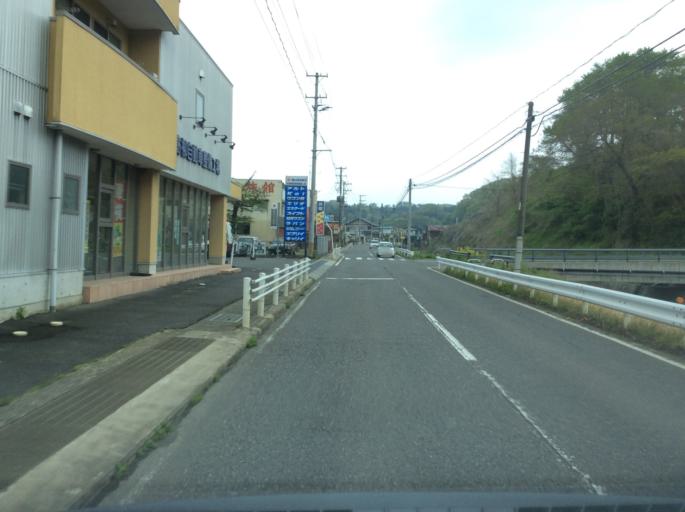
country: JP
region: Fukushima
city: Miharu
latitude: 37.4408
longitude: 140.4796
